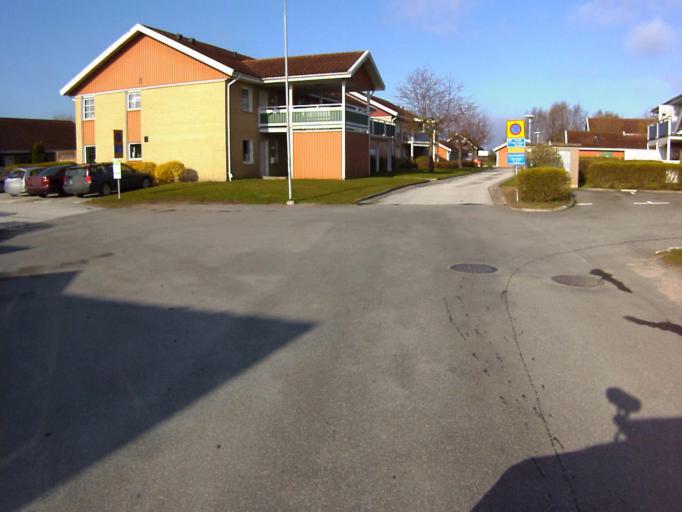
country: SE
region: Skane
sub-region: Kristianstads Kommun
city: Kristianstad
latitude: 56.0158
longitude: 14.1041
